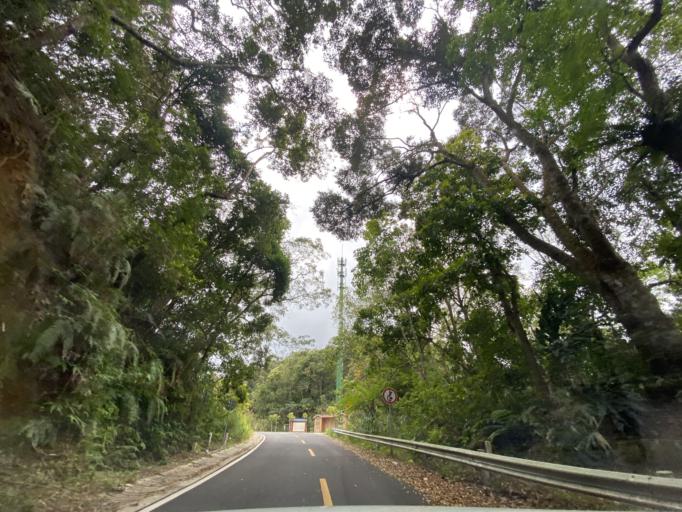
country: CN
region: Hainan
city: Diaoluoshan
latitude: 18.6991
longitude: 109.8811
